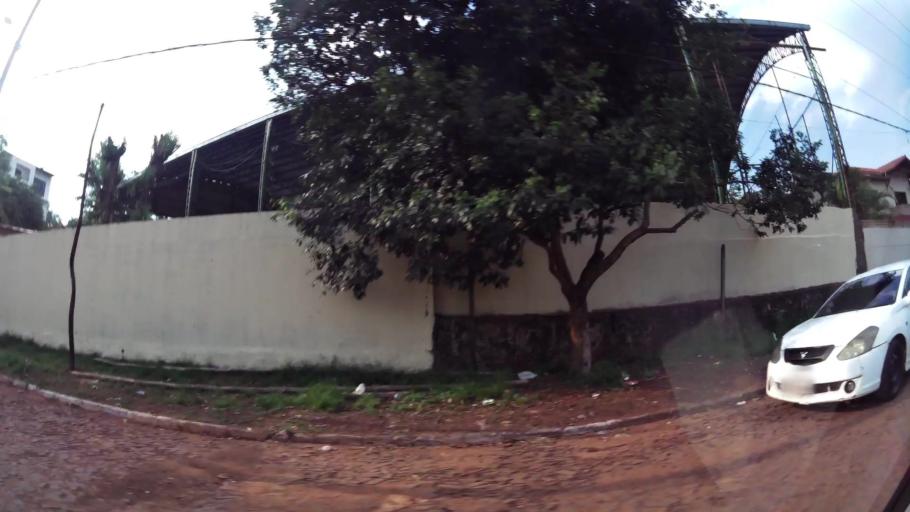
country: PY
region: Alto Parana
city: Presidente Franco
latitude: -25.5215
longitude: -54.6303
